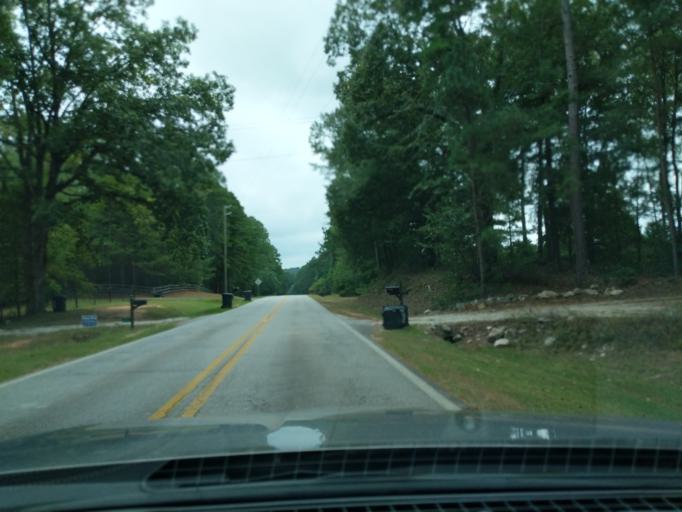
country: US
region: Georgia
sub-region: Columbia County
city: Appling
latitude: 33.5651
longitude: -82.3505
